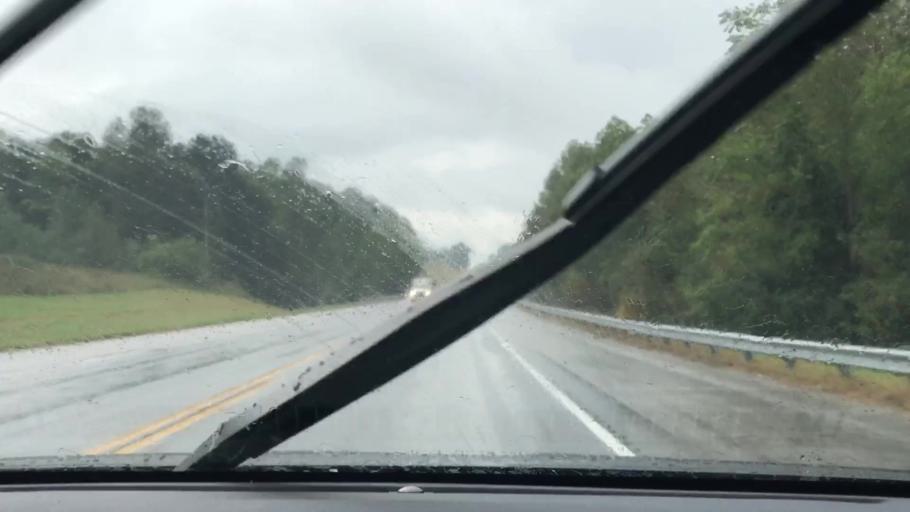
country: US
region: Tennessee
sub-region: Macon County
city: Lafayette
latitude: 36.5328
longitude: -86.0815
